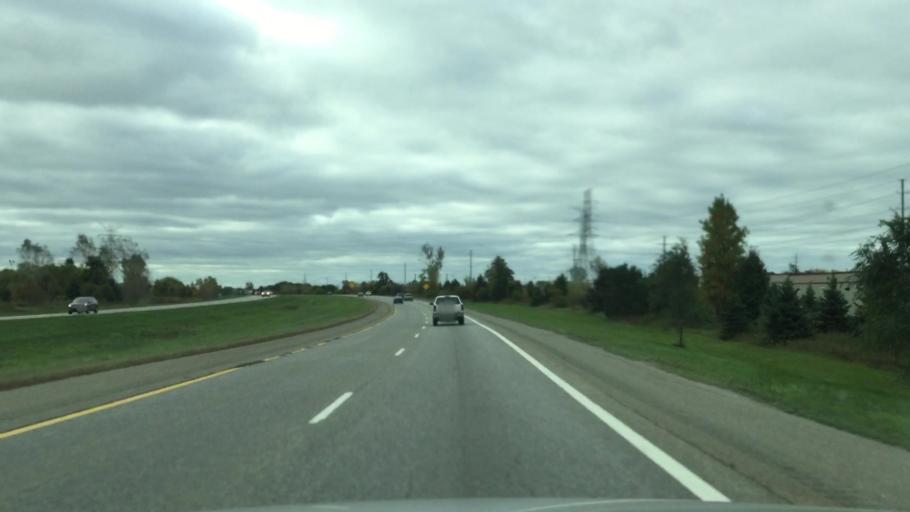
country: US
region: Michigan
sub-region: Macomb County
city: Romeo
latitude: 42.7833
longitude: -83.0078
